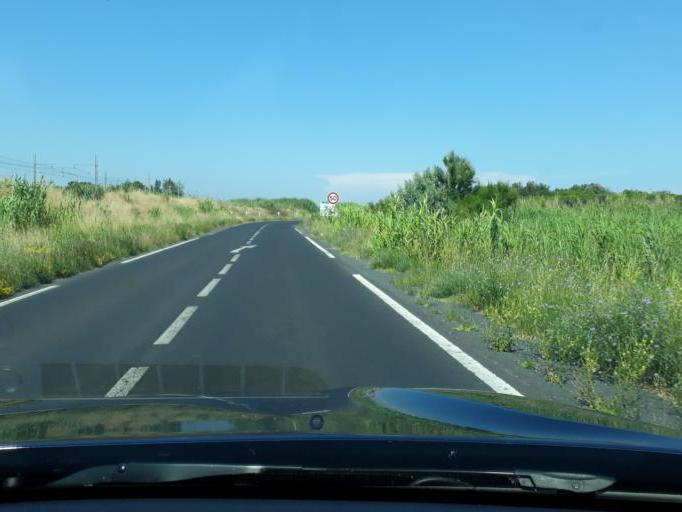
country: FR
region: Languedoc-Roussillon
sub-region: Departement de l'Herault
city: Marseillan
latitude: 43.3386
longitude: 3.5726
